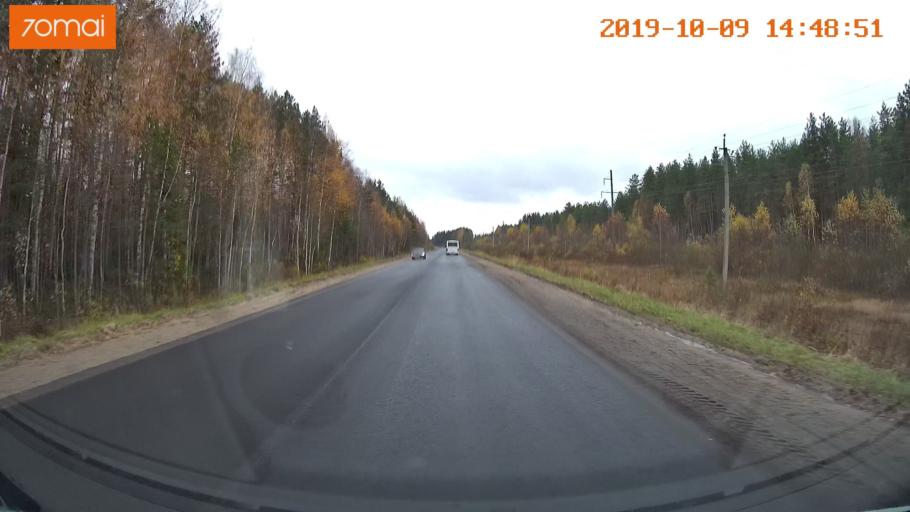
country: RU
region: Kostroma
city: Chistyye Bory
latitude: 58.4005
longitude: 41.5774
